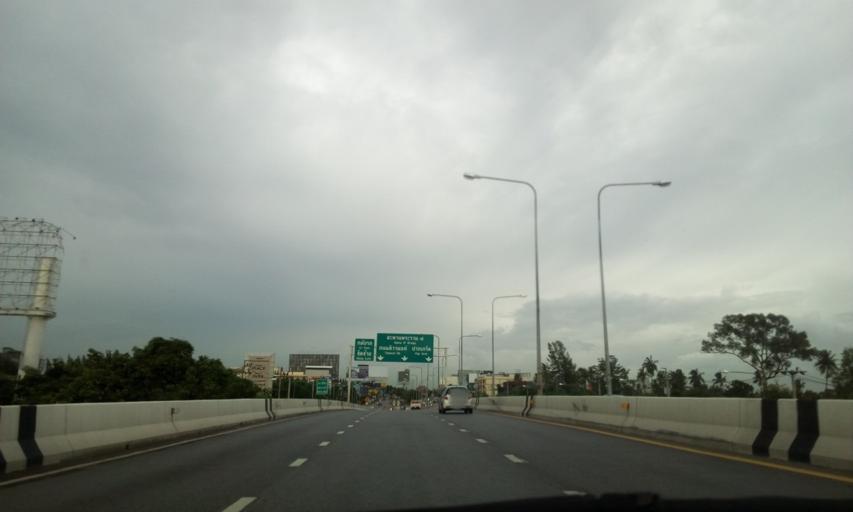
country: TH
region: Nonthaburi
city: Pak Kret
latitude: 13.9218
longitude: 100.4820
